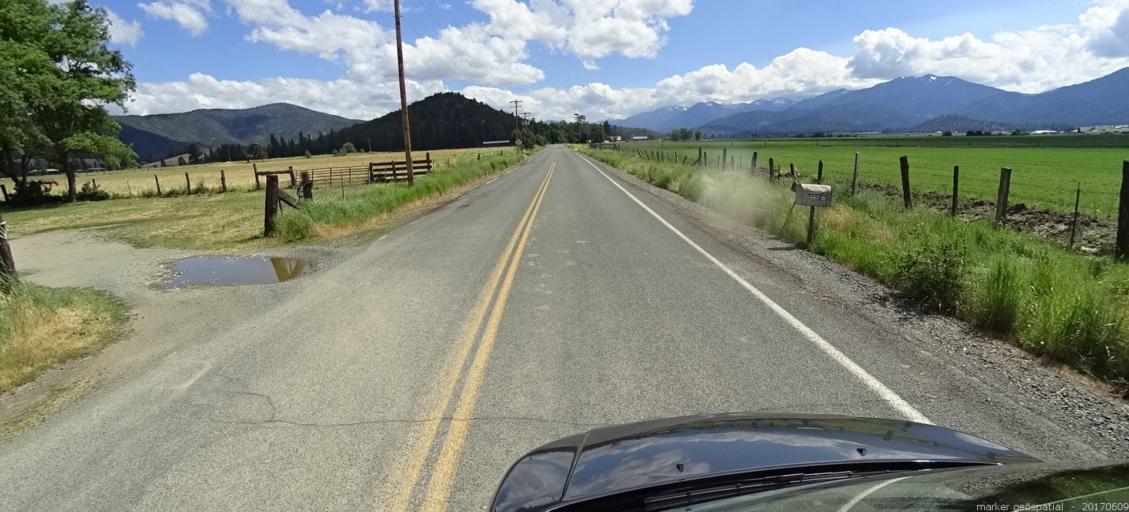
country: US
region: California
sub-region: Siskiyou County
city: Yreka
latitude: 41.5050
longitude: -122.8359
